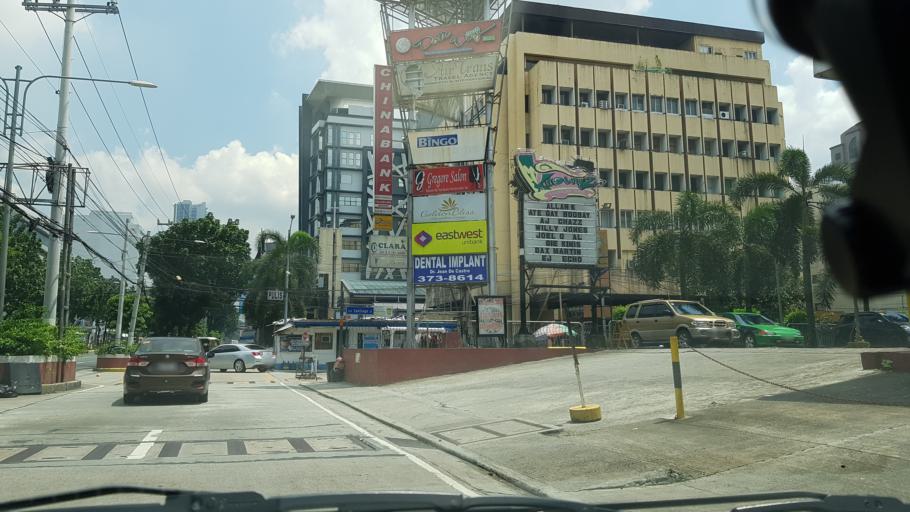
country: PH
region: Calabarzon
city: Del Monte
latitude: 14.6378
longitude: 121.0276
